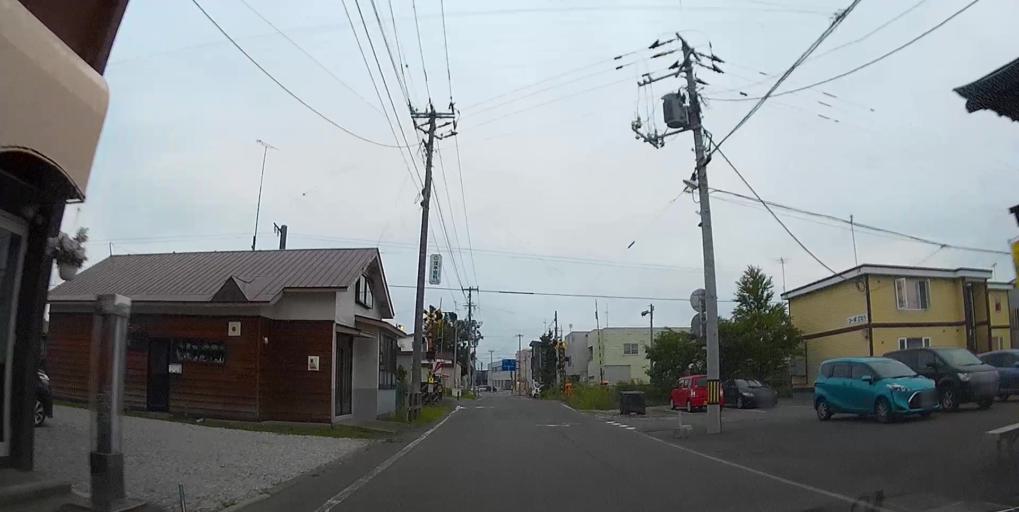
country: JP
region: Hokkaido
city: Nanae
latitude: 42.2564
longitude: 140.2669
